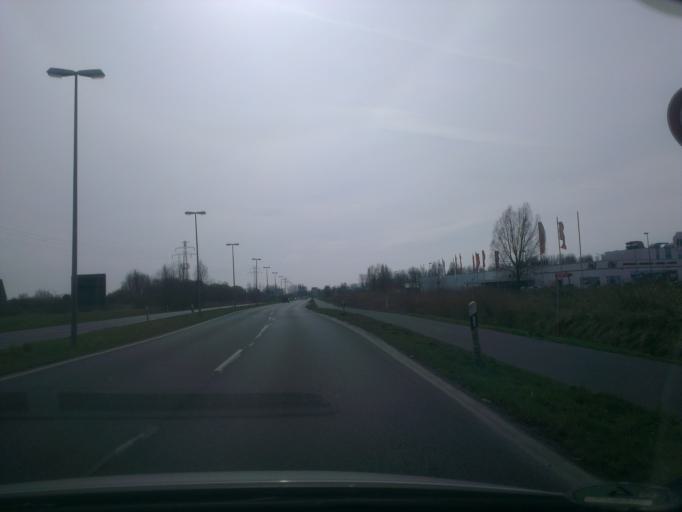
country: DE
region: Lower Saxony
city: Emden
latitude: 53.3639
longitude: 7.1724
